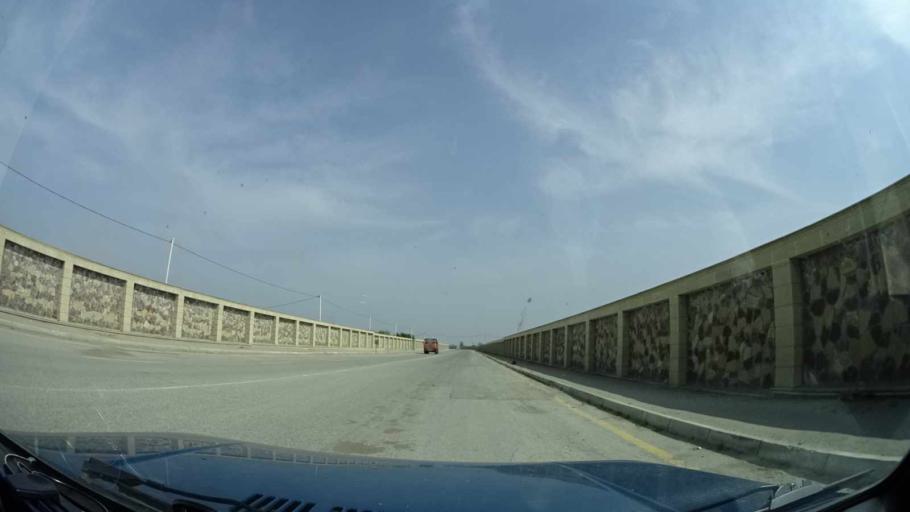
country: AZ
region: Xizi
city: Kilyazi
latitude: 40.8687
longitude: 49.3410
